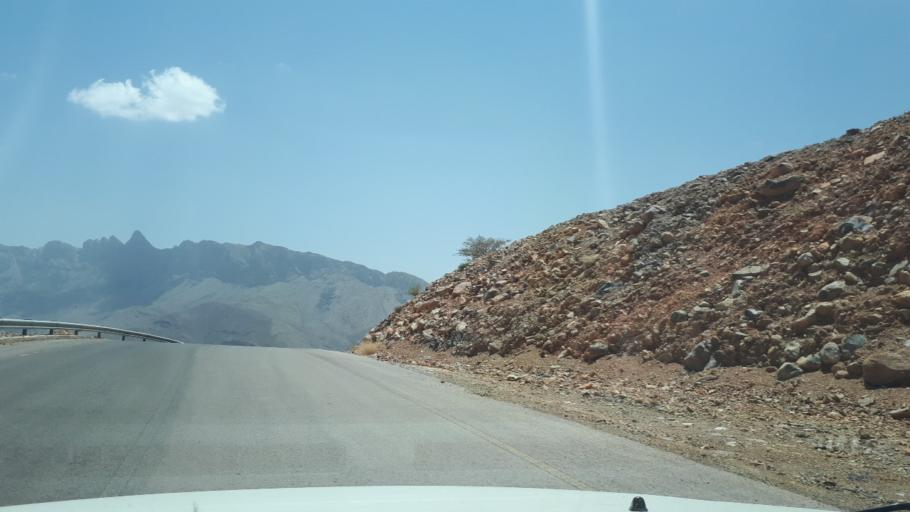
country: OM
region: Muhafazat ad Dakhiliyah
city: Bahla'
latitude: 23.2011
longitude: 57.1402
